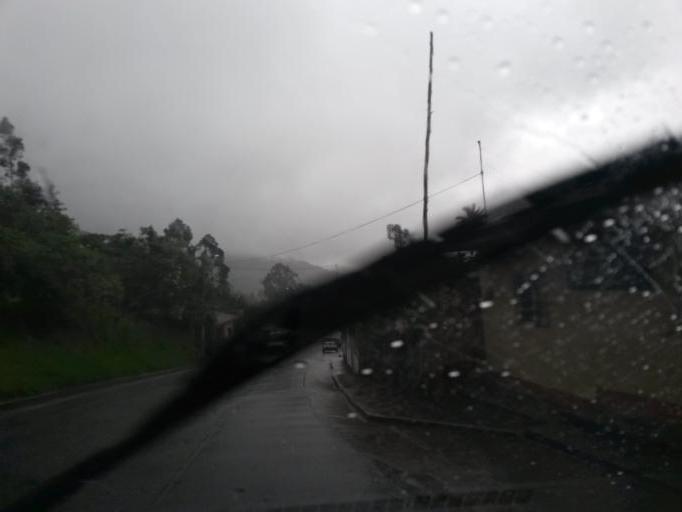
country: CO
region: Cauca
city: Paispamba
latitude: 2.3406
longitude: -76.4964
